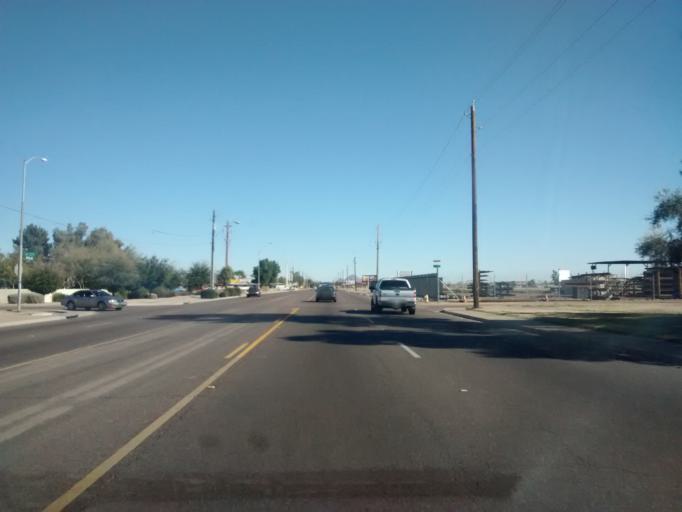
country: US
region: Arizona
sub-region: Maricopa County
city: Glendale
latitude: 33.5241
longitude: -112.1846
